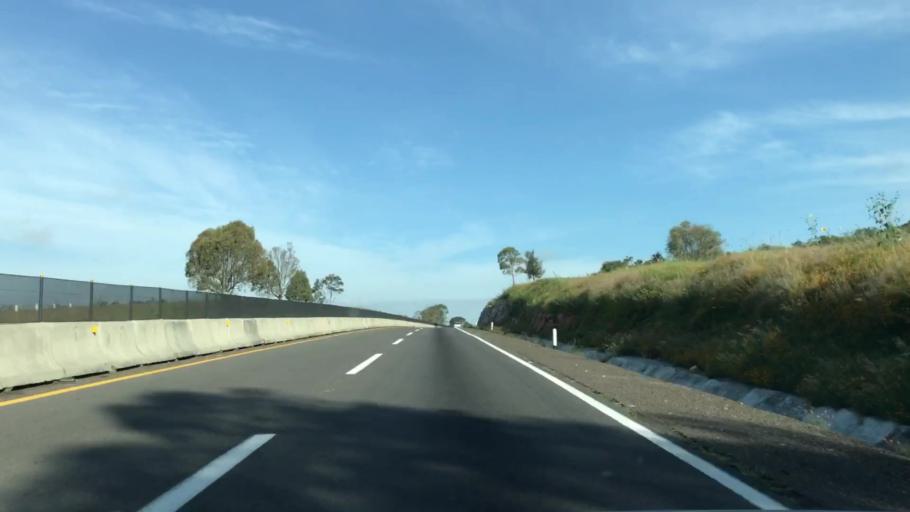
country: MX
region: Jalisco
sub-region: Lagos de Moreno
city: Cristeros [Fraccionamiento]
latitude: 21.3705
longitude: -102.1313
